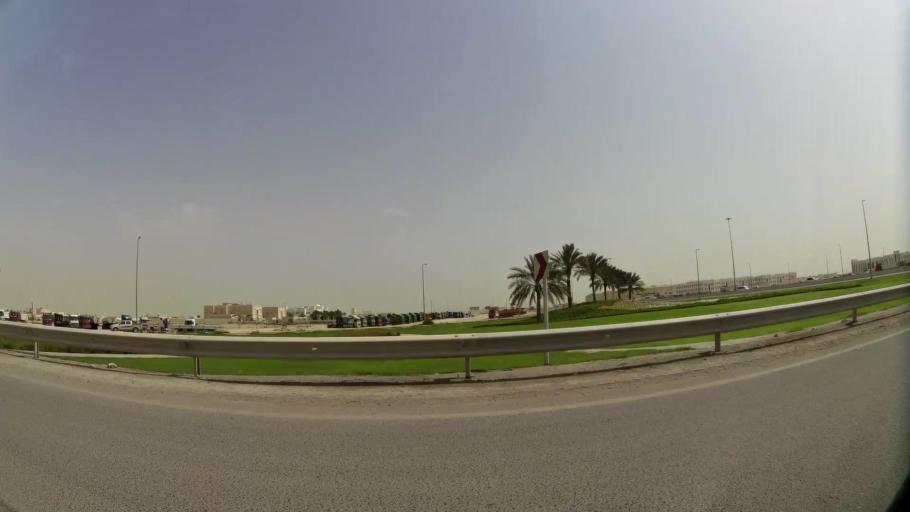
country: QA
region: Baladiyat ar Rayyan
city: Ar Rayyan
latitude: 25.2126
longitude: 51.4073
